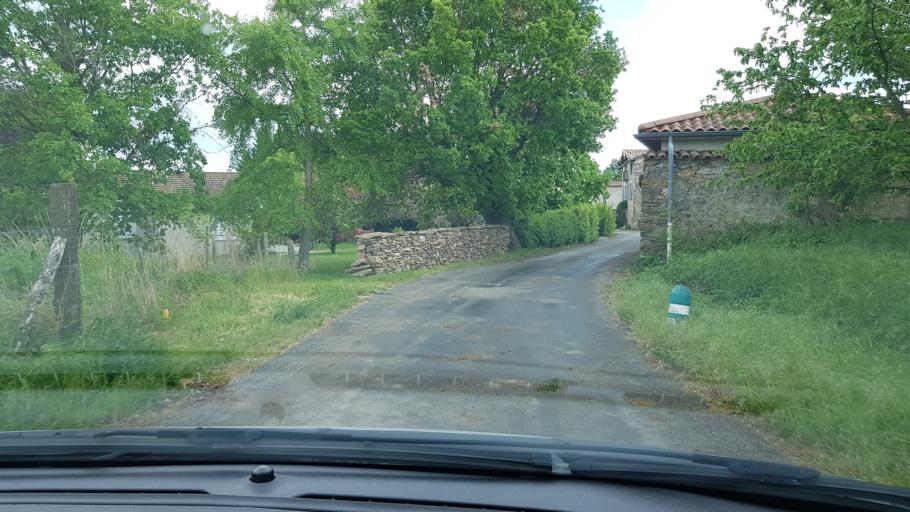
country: FR
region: Rhone-Alpes
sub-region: Departement du Rhone
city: Saint-Maurice-sur-Dargoire
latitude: 45.5784
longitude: 4.6435
